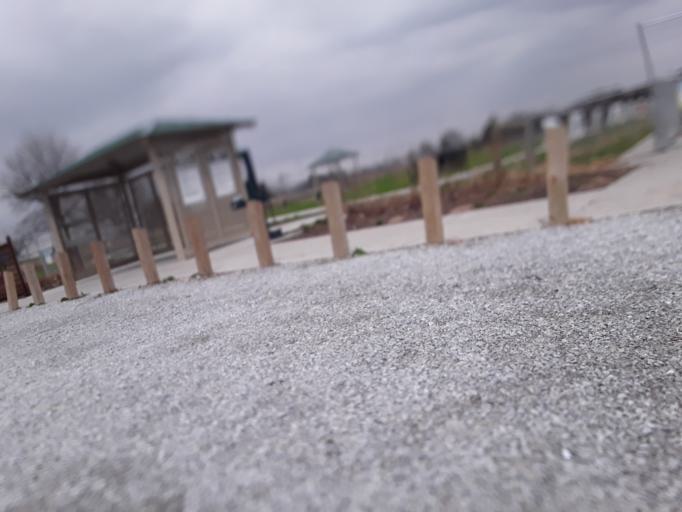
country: US
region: Nebraska
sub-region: Lancaster County
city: Lincoln
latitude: 40.8467
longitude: -96.6069
